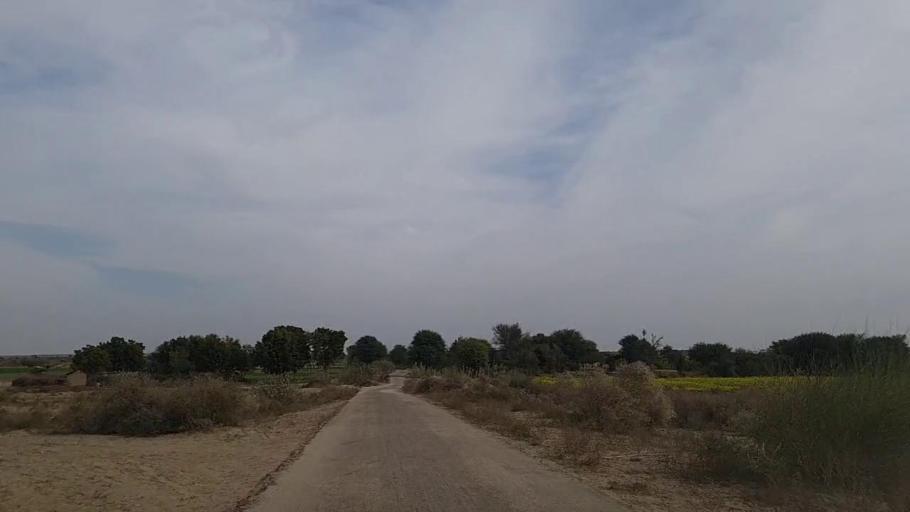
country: PK
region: Sindh
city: Jam Sahib
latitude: 26.4414
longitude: 68.6007
